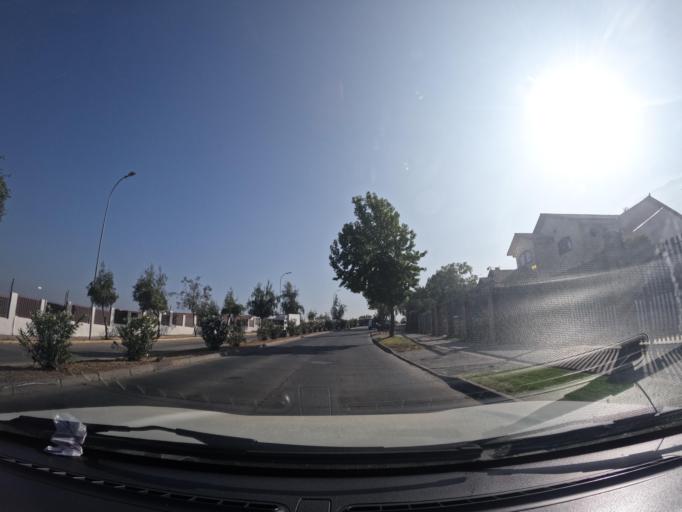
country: CL
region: Santiago Metropolitan
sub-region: Provincia de Santiago
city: Villa Presidente Frei, Nunoa, Santiago, Chile
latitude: -33.4655
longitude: -70.5229
